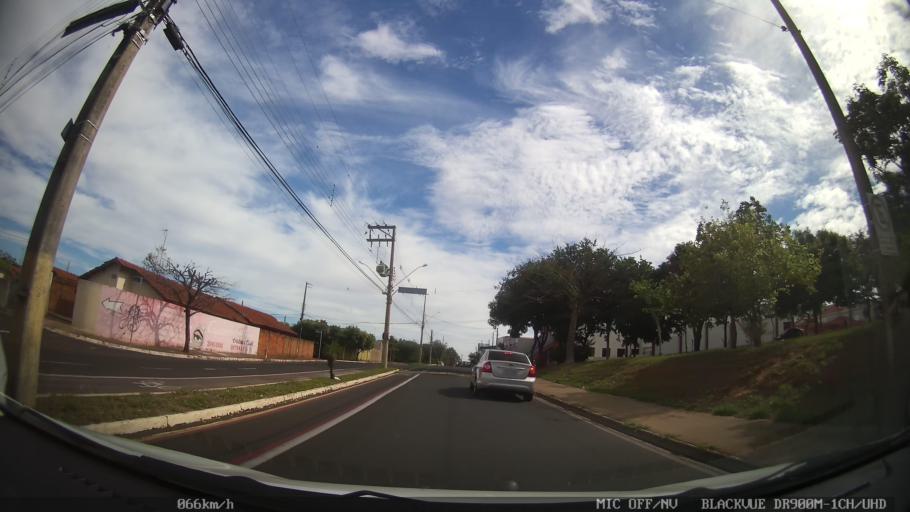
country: BR
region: Sao Paulo
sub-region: Catanduva
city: Catanduva
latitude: -21.1421
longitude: -48.9513
